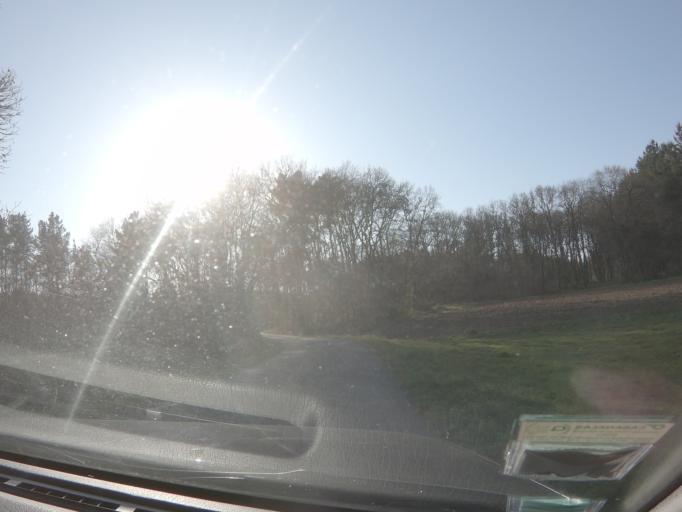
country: ES
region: Galicia
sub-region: Provincia de Lugo
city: Corgo
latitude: 42.9401
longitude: -7.4406
